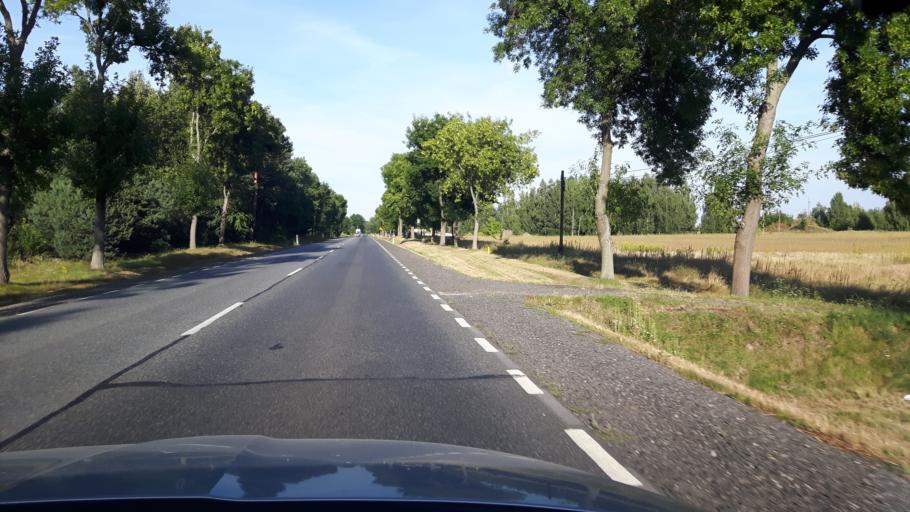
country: PL
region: Masovian Voivodeship
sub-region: Powiat nowodworski
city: Brody-Parcele
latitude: 52.4932
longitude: 20.8376
